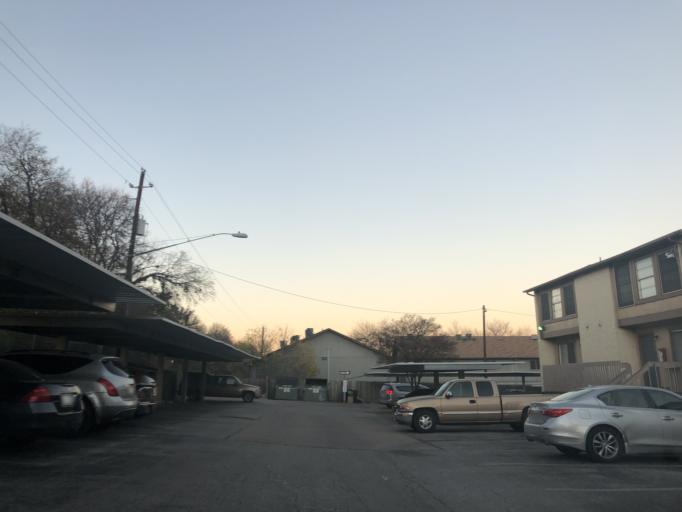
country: US
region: Texas
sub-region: Travis County
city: Austin
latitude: 30.2324
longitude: -97.7343
